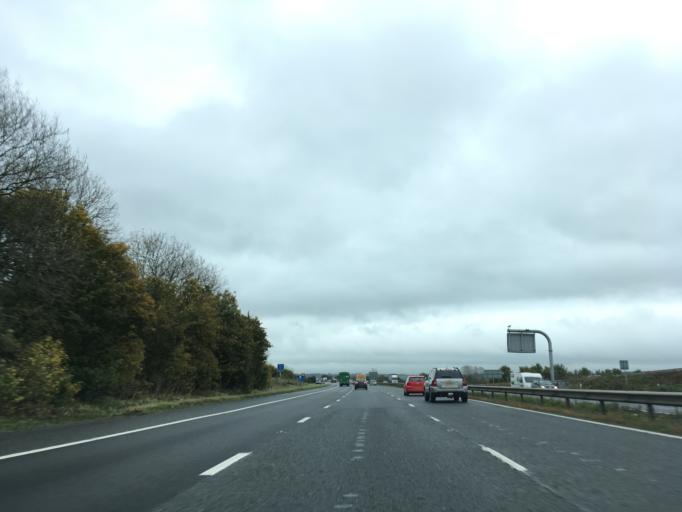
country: GB
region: England
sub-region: Wiltshire
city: Lydiard Tregoze
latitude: 51.5450
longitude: -1.8521
